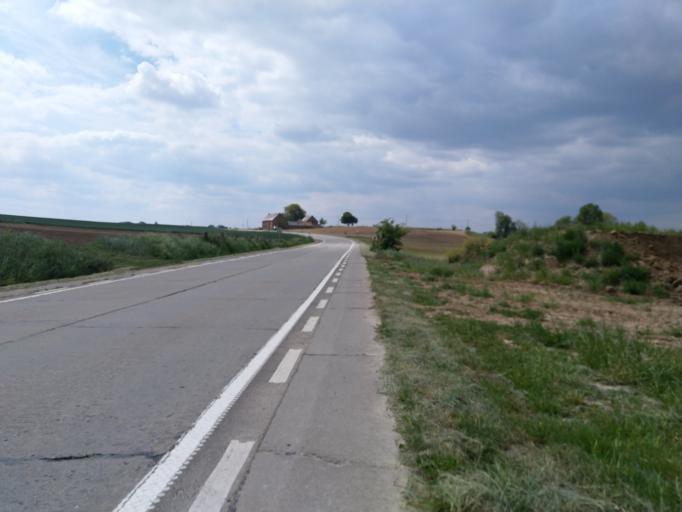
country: BE
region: Wallonia
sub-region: Province du Hainaut
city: Lens
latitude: 50.5749
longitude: 3.9162
